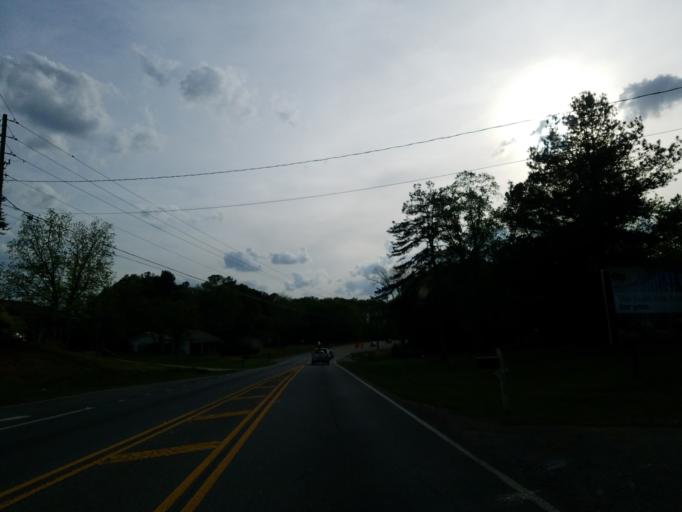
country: US
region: Georgia
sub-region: Cherokee County
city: Ball Ground
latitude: 34.2522
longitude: -84.3648
